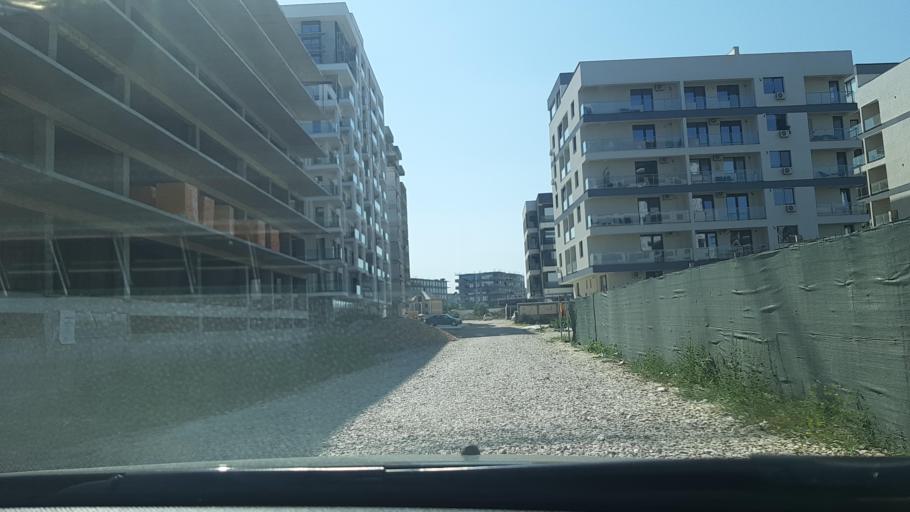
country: RO
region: Constanta
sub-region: Comuna Navodari
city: Navodari
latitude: 44.3073
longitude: 28.6267
